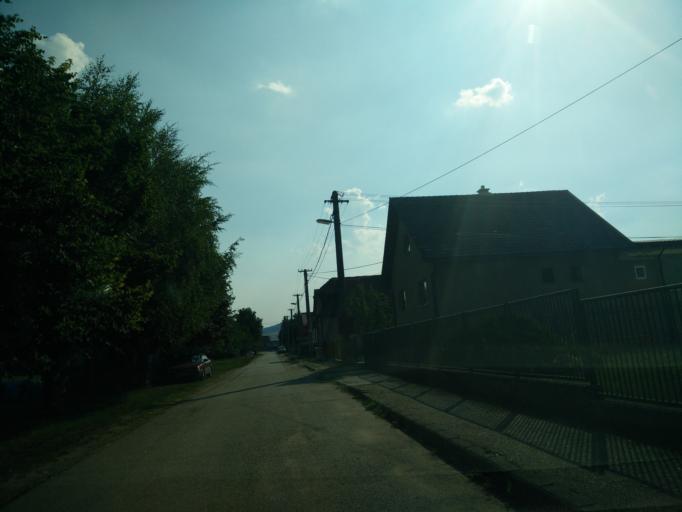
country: SK
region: Zilinsky
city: Rajec
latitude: 49.1209
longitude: 18.6534
